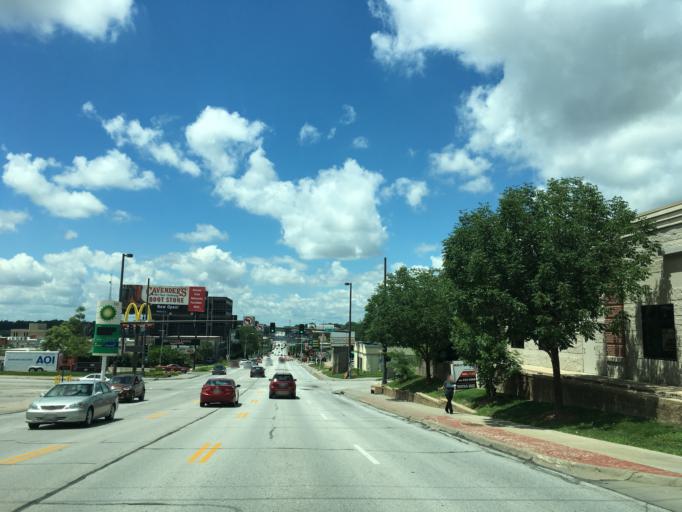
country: US
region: Nebraska
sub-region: Douglas County
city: Omaha
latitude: 41.2597
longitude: -95.9724
